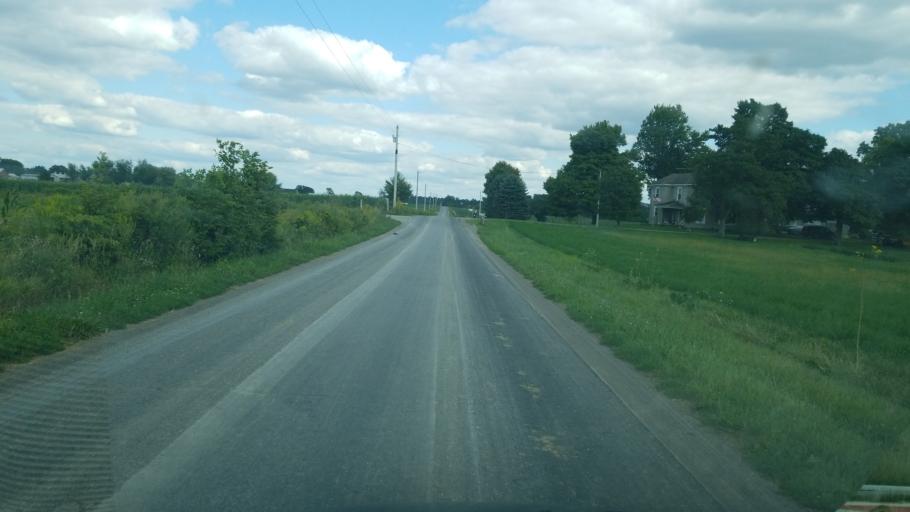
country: US
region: Ohio
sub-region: Logan County
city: De Graff
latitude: 40.3767
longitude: -83.8949
